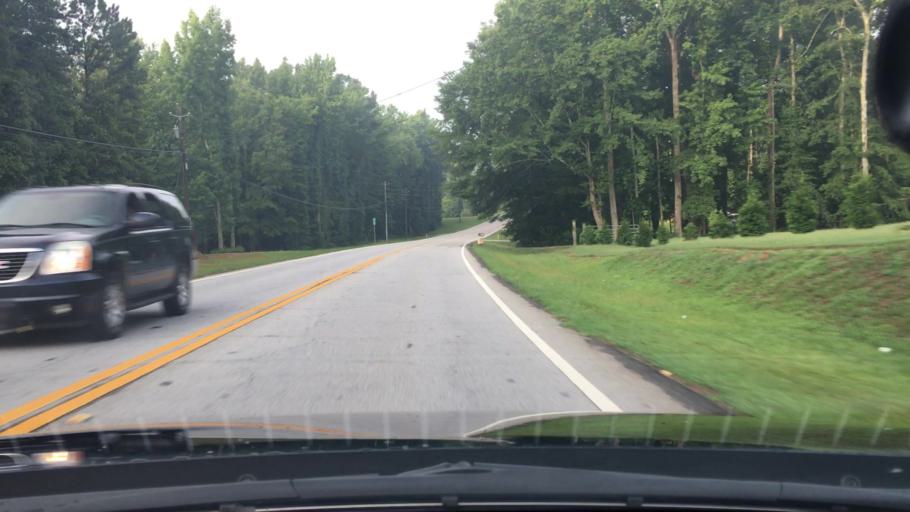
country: US
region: Georgia
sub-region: Fayette County
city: Peachtree City
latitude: 33.3545
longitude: -84.6369
